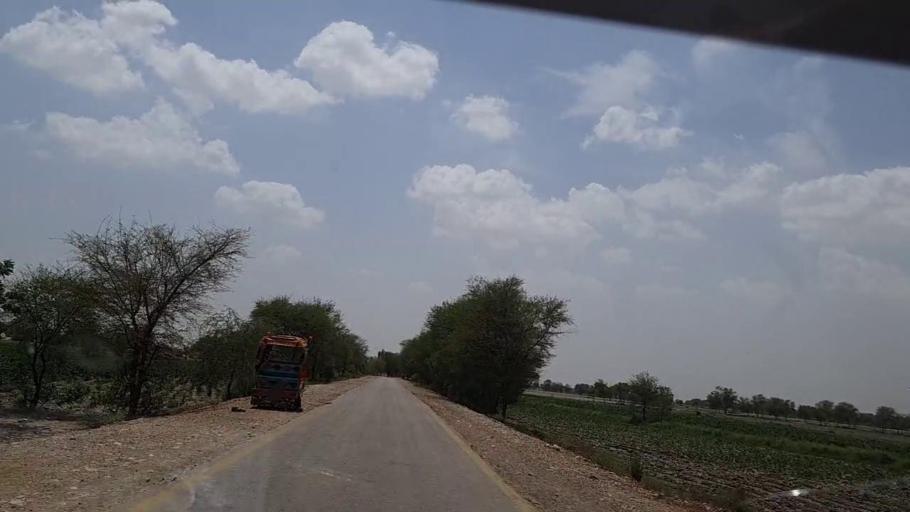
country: PK
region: Sindh
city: Bhan
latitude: 26.5409
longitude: 67.6776
